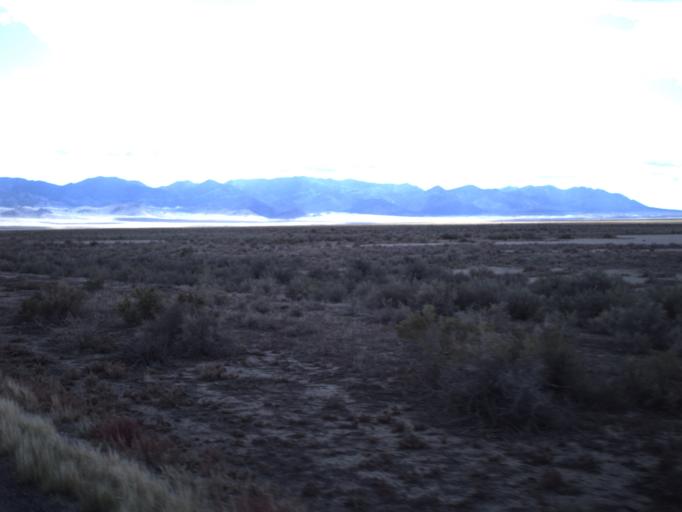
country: US
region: Utah
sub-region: Beaver County
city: Milford
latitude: 38.5423
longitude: -113.7089
